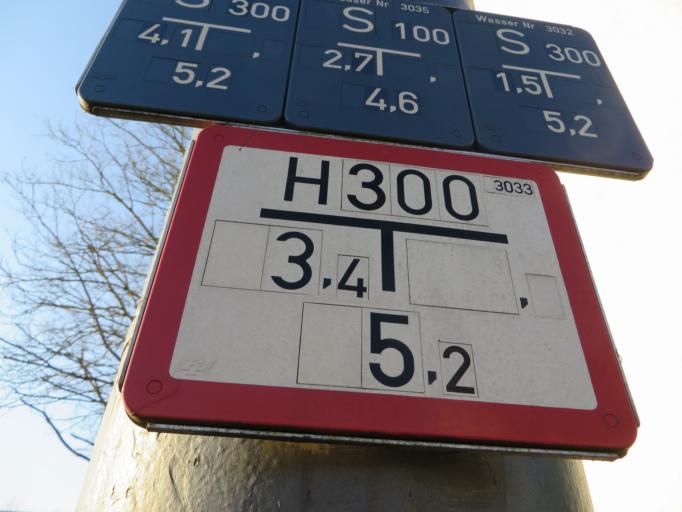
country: DE
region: North Rhine-Westphalia
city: Witten
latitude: 51.4446
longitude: 7.3560
